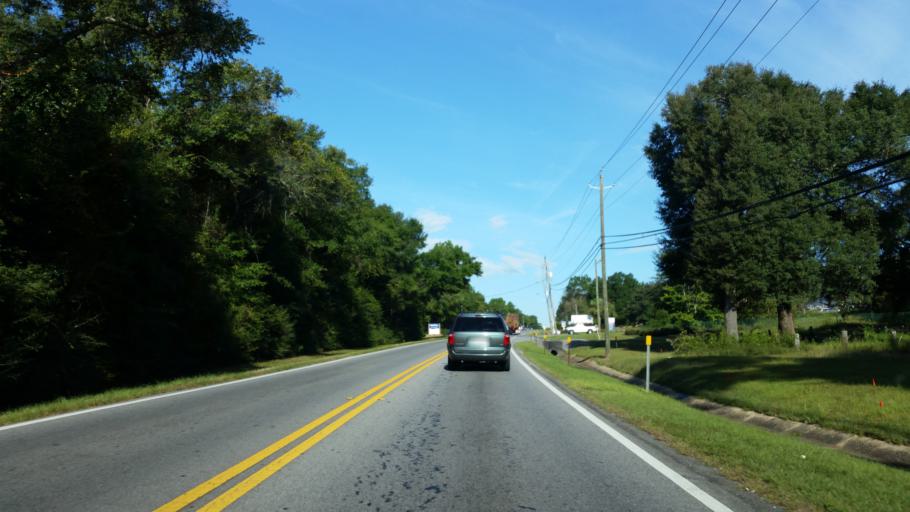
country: US
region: Florida
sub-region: Santa Rosa County
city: Milton
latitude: 30.6318
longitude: -87.0665
